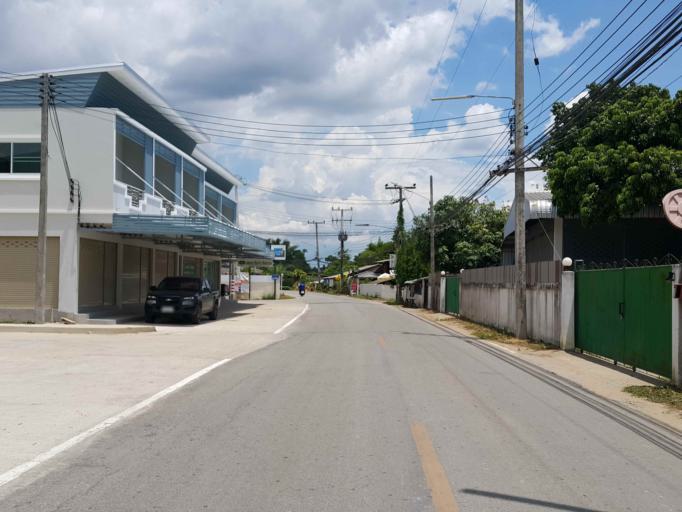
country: TH
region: Chiang Mai
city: Saraphi
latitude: 18.7342
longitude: 98.9963
